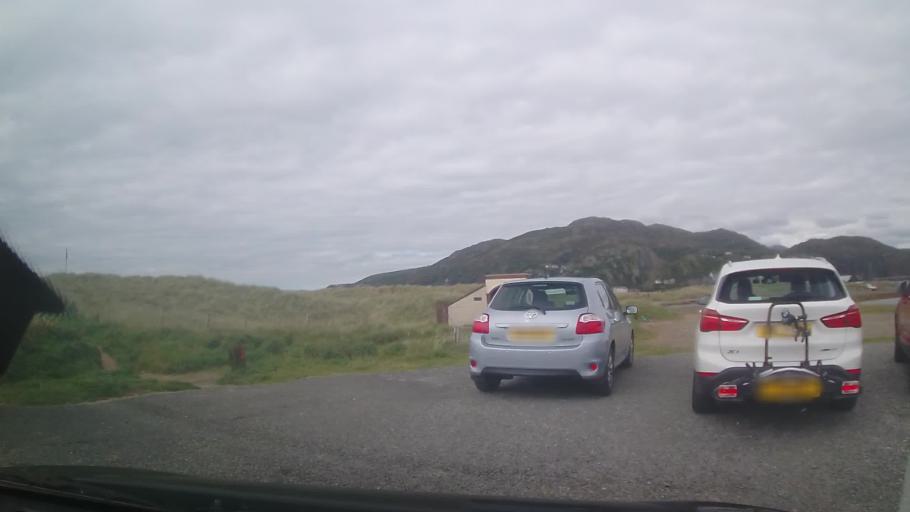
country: GB
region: Wales
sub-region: Gwynedd
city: Barmouth
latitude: 52.7122
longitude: -4.0519
